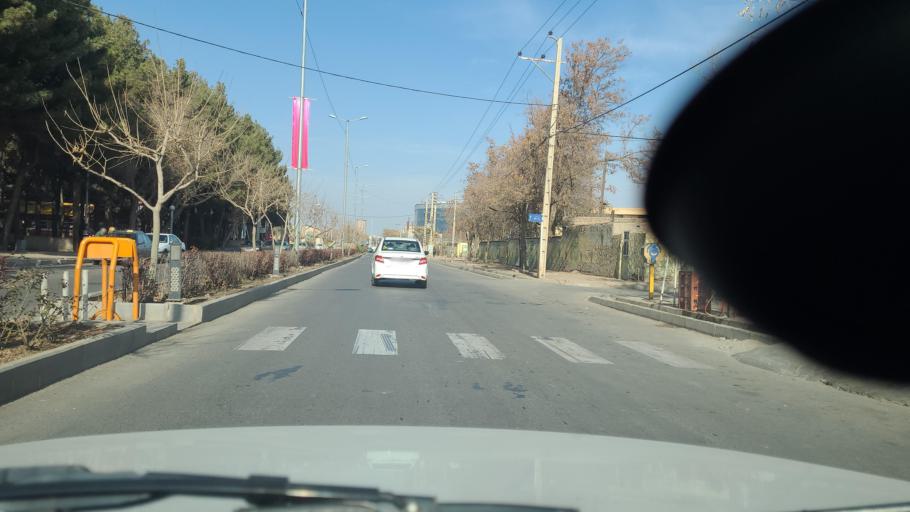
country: IR
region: Razavi Khorasan
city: Fariman
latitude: 35.6928
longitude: 59.8442
